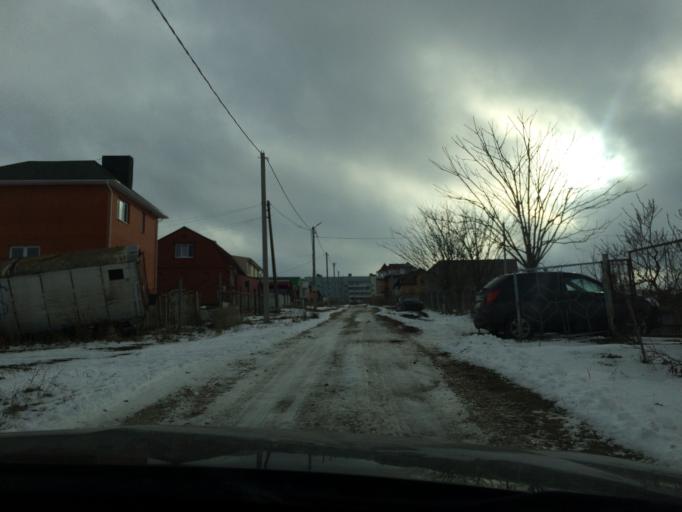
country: RU
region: Tula
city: Plavsk
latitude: 53.7060
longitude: 37.2716
